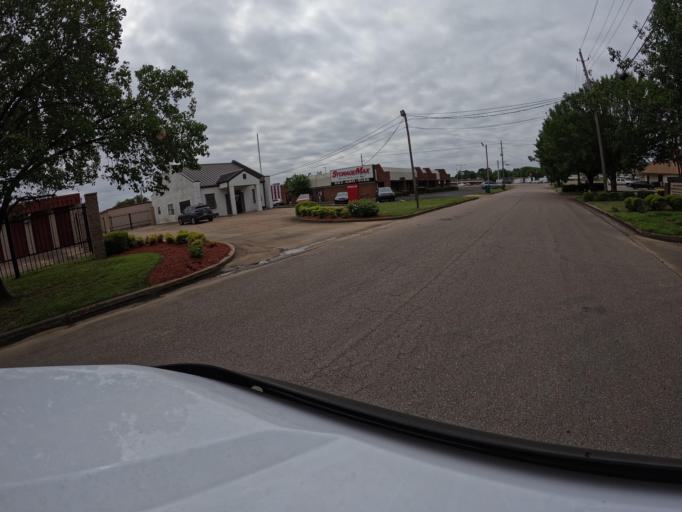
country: US
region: Mississippi
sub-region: Lee County
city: Tupelo
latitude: 34.2558
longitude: -88.7490
